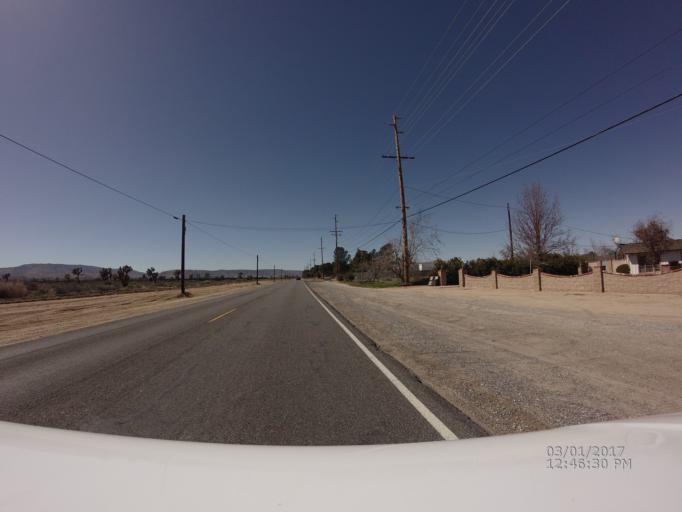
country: US
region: California
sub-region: Los Angeles County
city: Desert View Highlands
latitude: 34.6458
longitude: -118.1580
